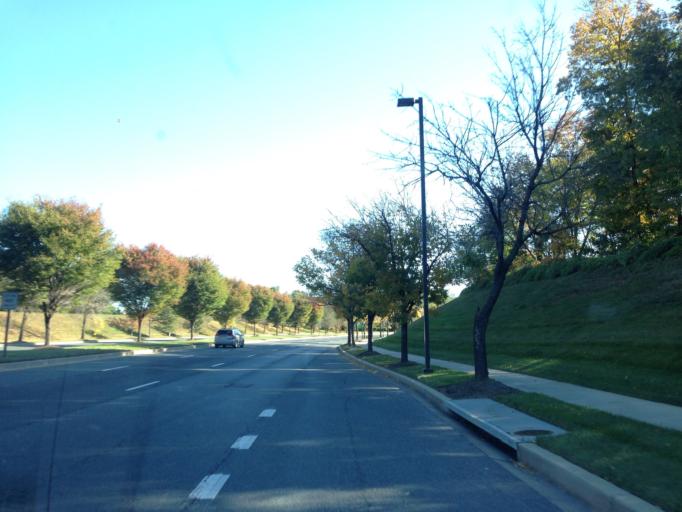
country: US
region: Maryland
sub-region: Montgomery County
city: Germantown
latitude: 39.2032
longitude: -77.2504
